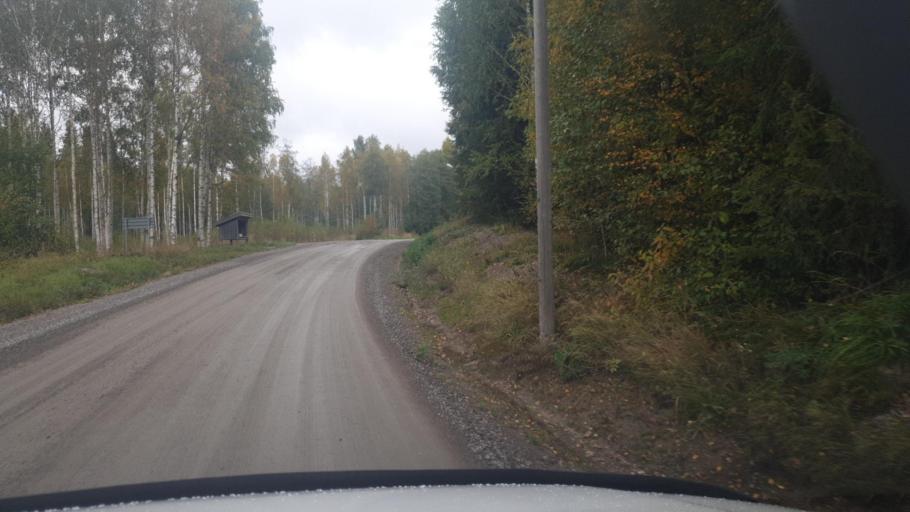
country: SE
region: Vaermland
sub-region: Arvika Kommun
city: Arvika
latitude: 59.9407
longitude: 12.6603
